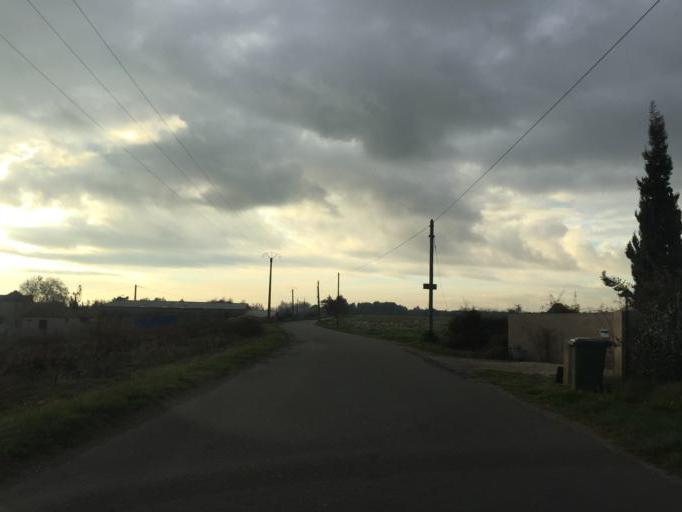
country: FR
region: Provence-Alpes-Cote d'Azur
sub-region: Departement du Vaucluse
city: Jonquieres
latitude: 44.1221
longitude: 4.8764
